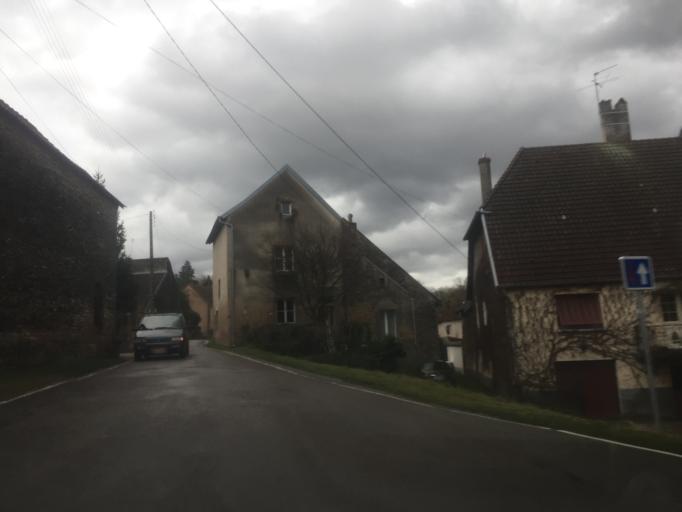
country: FR
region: Franche-Comte
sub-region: Departement de la Haute-Saone
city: Pesmes
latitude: 47.2179
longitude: 5.5208
